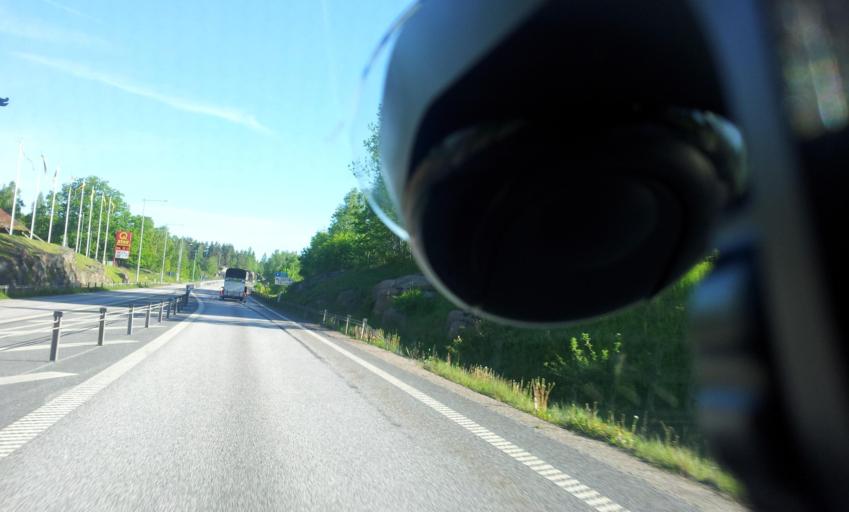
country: SE
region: Kalmar
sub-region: Vasterviks Kommun
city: Forserum
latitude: 57.9780
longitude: 16.4843
